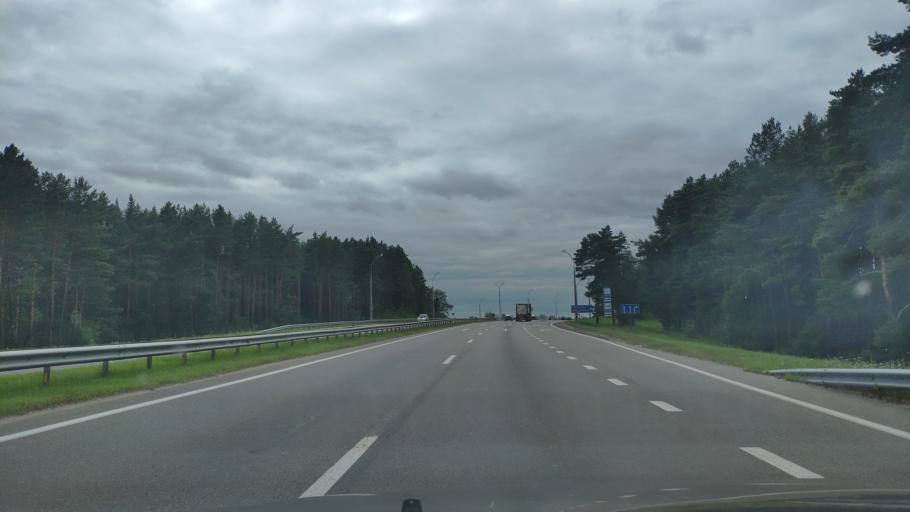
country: BY
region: Minsk
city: Zhdanovichy
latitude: 53.9461
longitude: 27.3611
